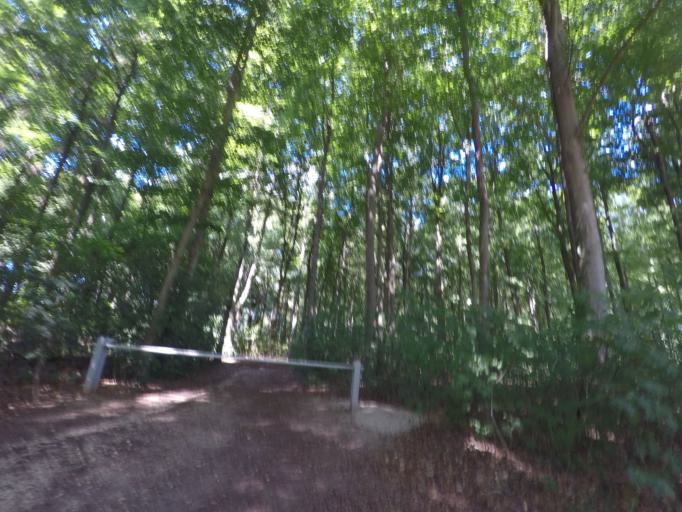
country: LU
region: Luxembourg
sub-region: Canton de Luxembourg
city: Strassen
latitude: 49.6375
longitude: 6.0656
